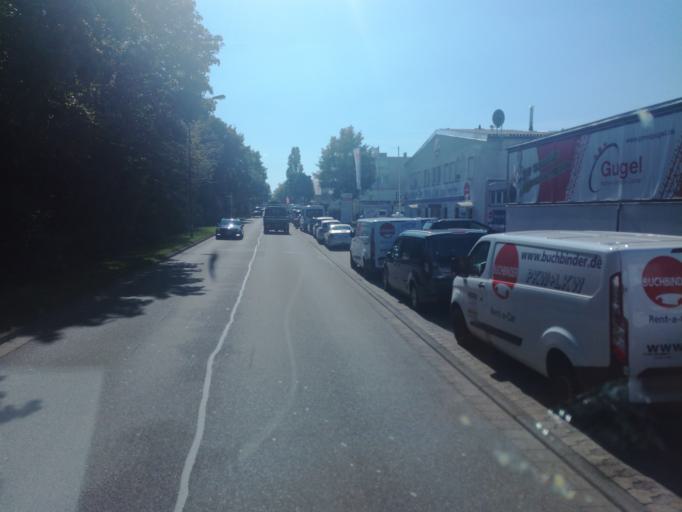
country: DE
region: Baden-Wuerttemberg
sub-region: Freiburg Region
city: Gundelfingen
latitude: 48.0284
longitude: 7.8581
